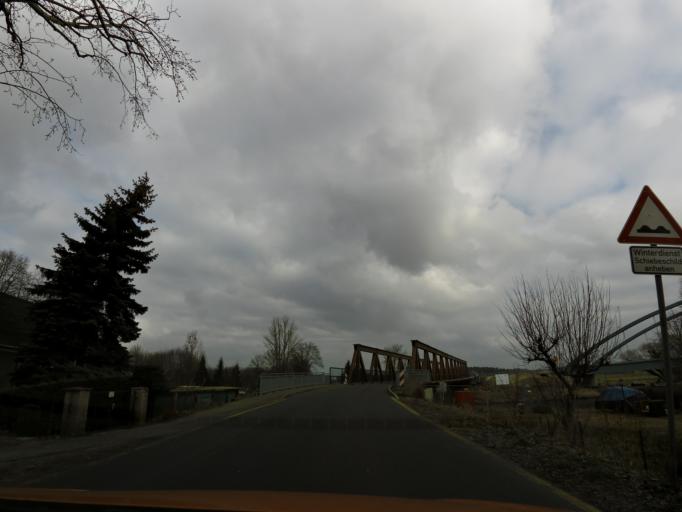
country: DE
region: Brandenburg
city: Werder
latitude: 52.4510
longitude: 12.9786
